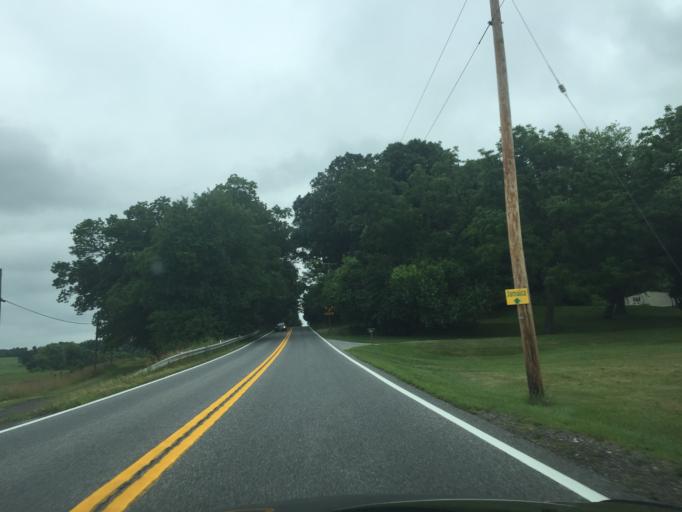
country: US
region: Maryland
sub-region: Harford County
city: Jarrettsville
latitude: 39.5480
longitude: -76.5285
